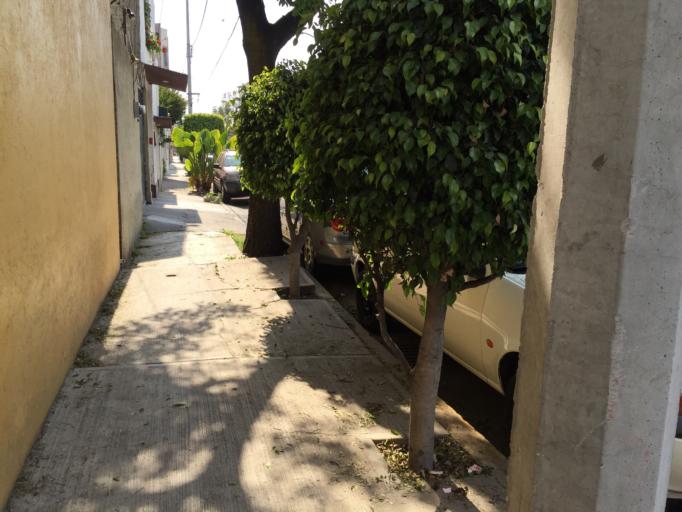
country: MX
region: Mexico
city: Colonia Lindavista
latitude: 19.5006
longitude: -99.1266
